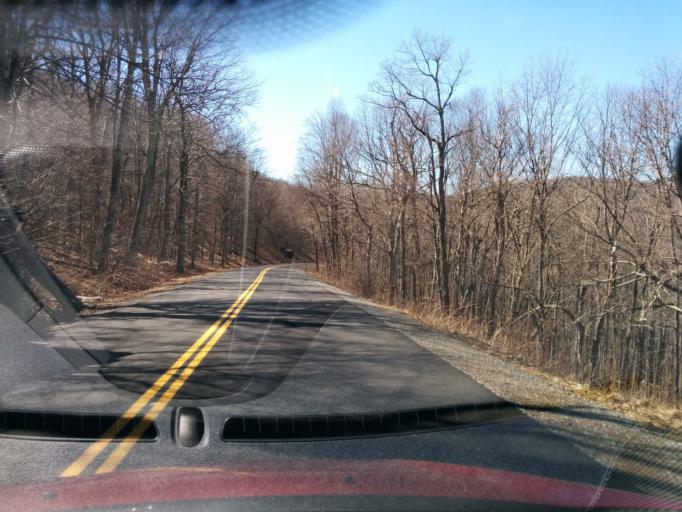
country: US
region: Virginia
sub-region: Augusta County
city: Stuarts Draft
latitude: 37.8946
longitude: -79.0373
